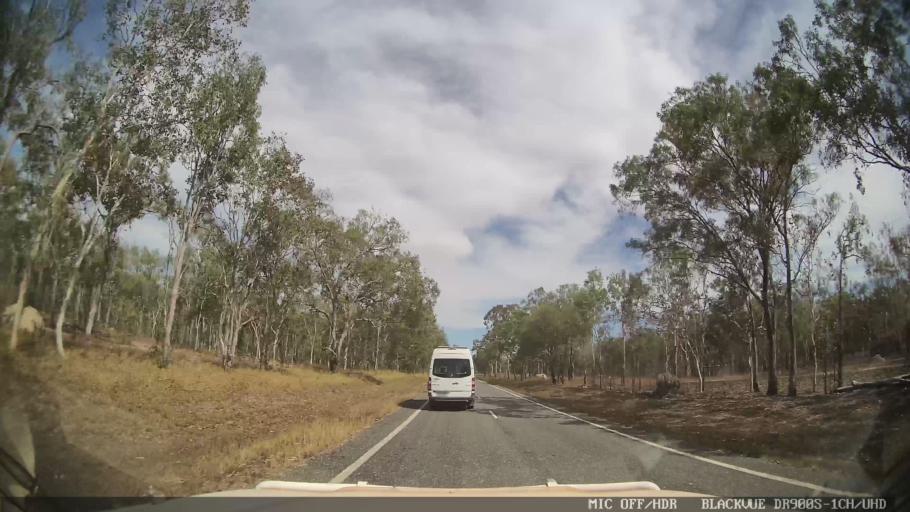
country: AU
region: Queensland
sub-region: Cairns
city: Port Douglas
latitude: -16.7257
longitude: 145.3528
